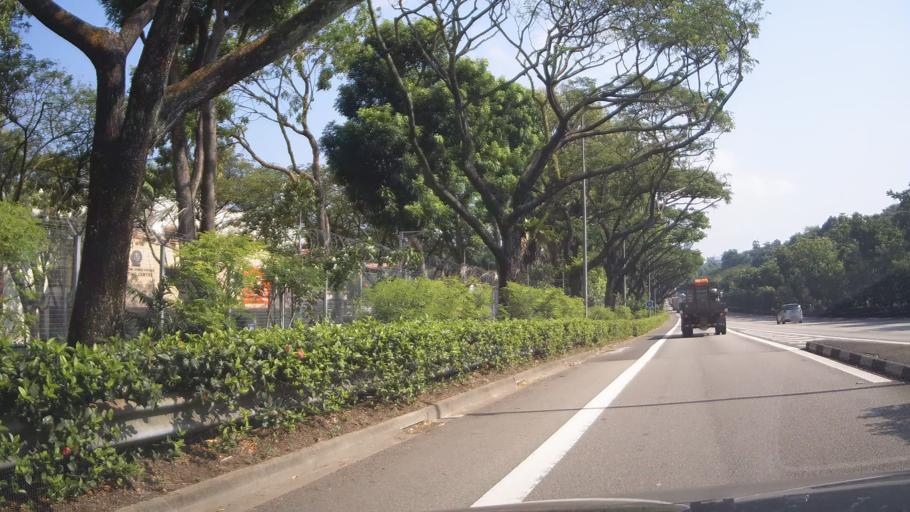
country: MY
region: Johor
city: Johor Bahru
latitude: 1.3329
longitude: 103.6756
